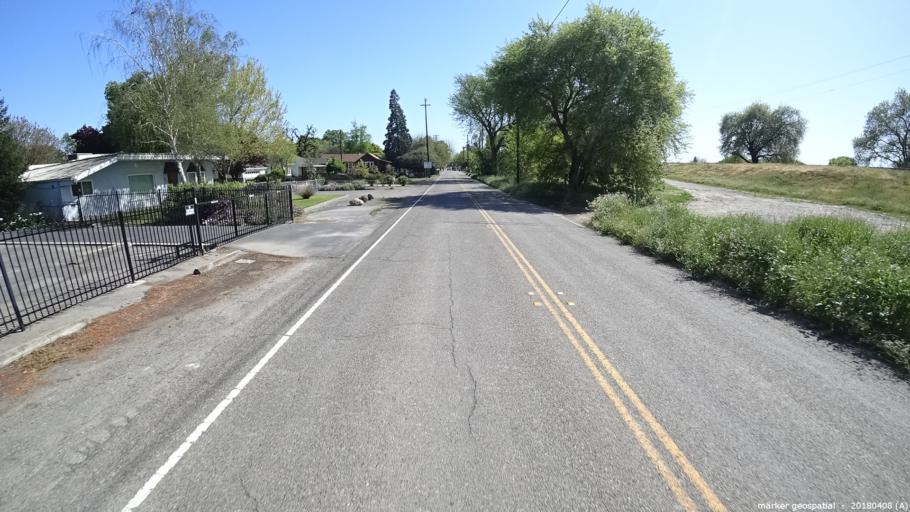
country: US
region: California
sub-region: Sacramento County
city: Parkway
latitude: 38.4643
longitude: -121.5026
